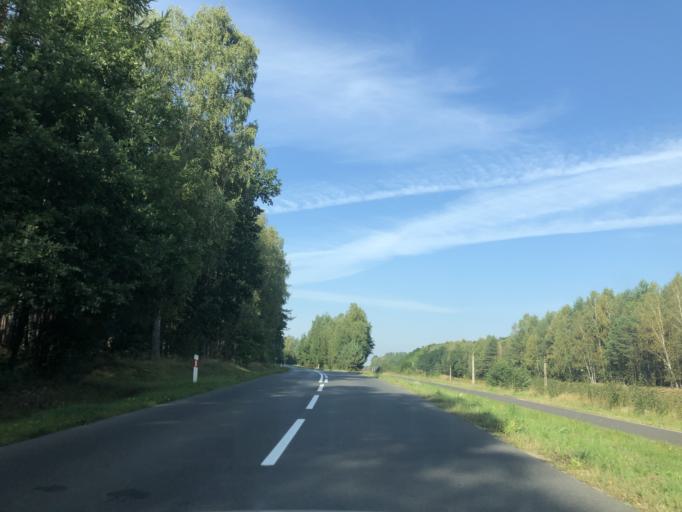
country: PL
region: Greater Poland Voivodeship
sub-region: Powiat pilski
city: Kaczory
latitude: 53.1267
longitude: 16.8114
